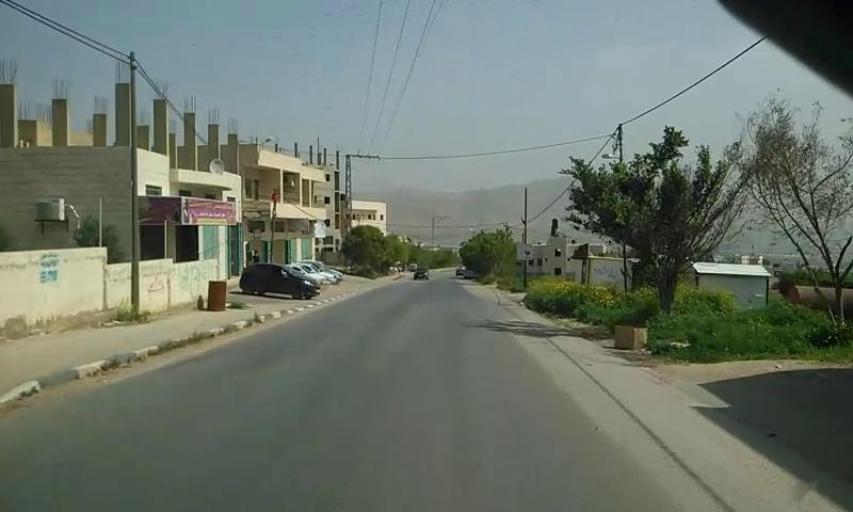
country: PS
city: Al Badhan
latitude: 32.2618
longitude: 35.3302
